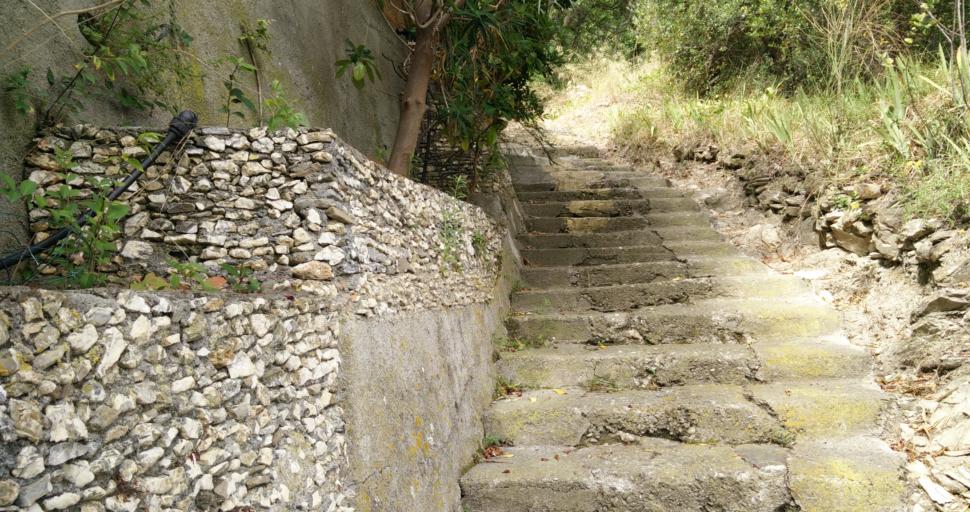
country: IT
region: Liguria
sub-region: Provincia di Savona
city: Alassio
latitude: 43.9976
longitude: 8.1635
